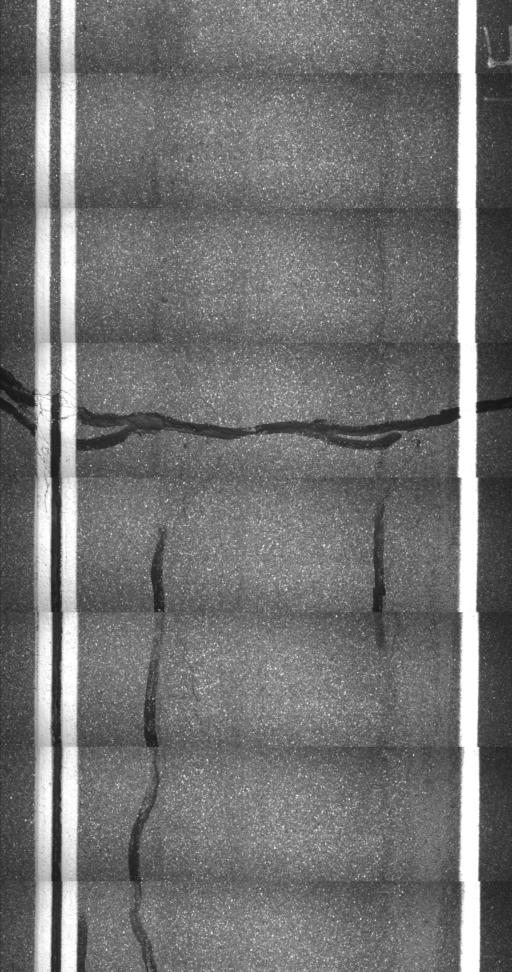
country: US
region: Massachusetts
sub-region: Berkshire County
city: North Adams
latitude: 42.7867
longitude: -73.0383
